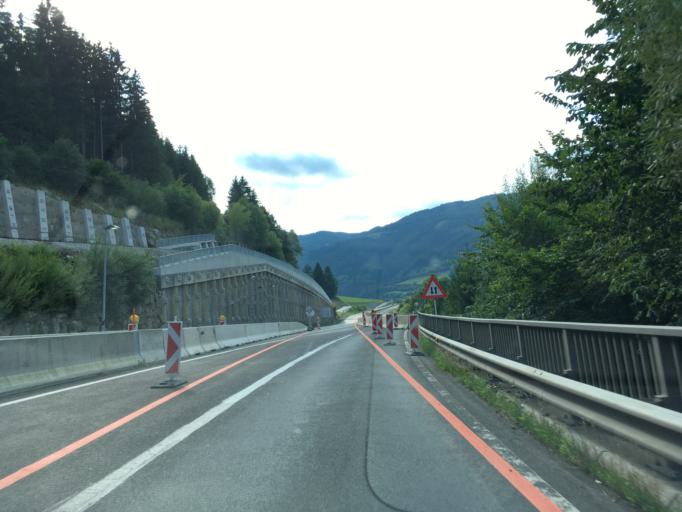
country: AT
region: Styria
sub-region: Politischer Bezirk Murtal
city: Sankt Georgen ob Judenburg
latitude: 47.2077
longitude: 14.4858
